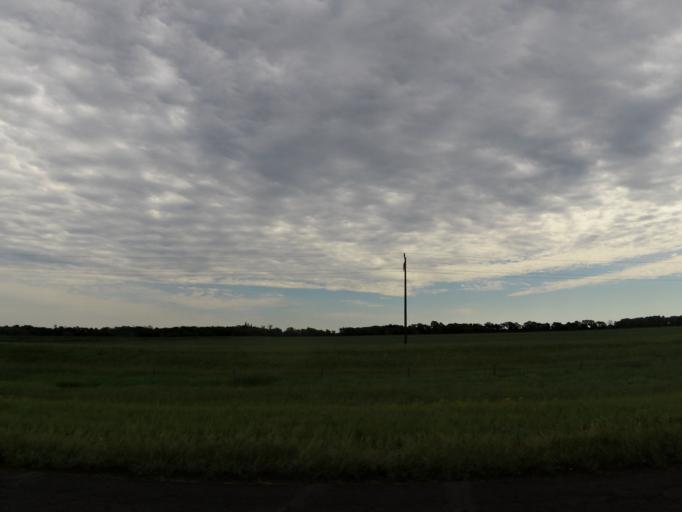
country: US
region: North Dakota
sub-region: Walsh County
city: Grafton
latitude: 48.2502
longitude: -97.1890
